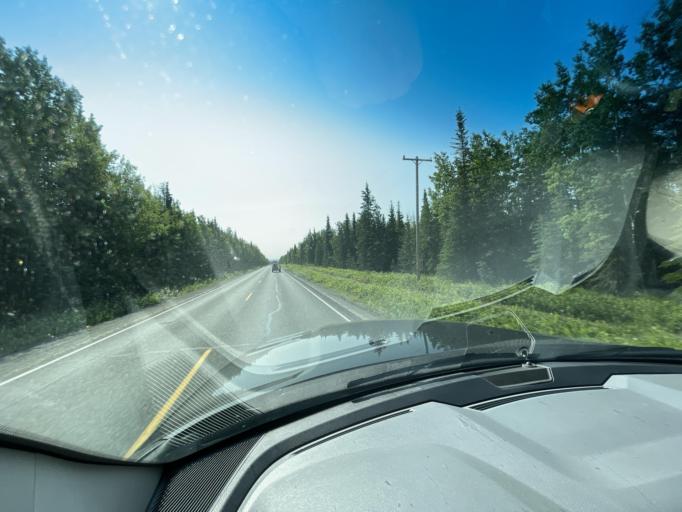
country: US
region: Alaska
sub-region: Kenai Peninsula Borough
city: Cohoe
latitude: 60.3091
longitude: -151.2903
